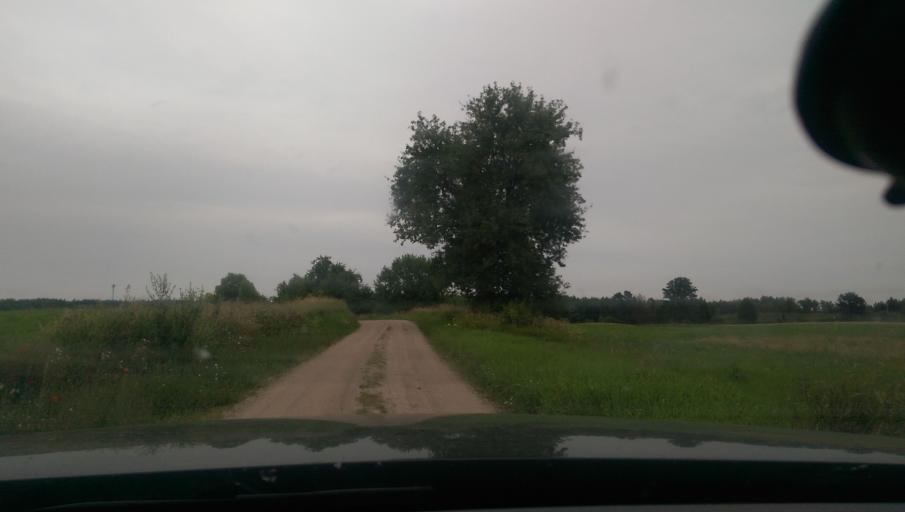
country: PL
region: Warmian-Masurian Voivodeship
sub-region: Powiat piski
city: Orzysz
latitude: 53.8164
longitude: 21.8044
